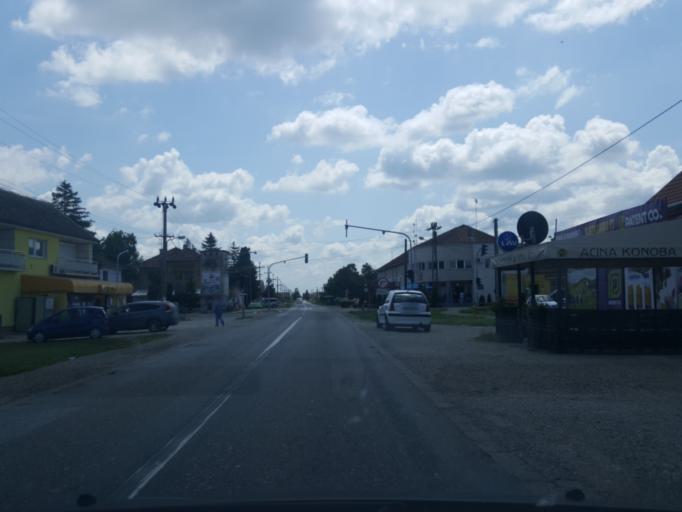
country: RS
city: Glusci
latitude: 44.8905
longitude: 19.5485
